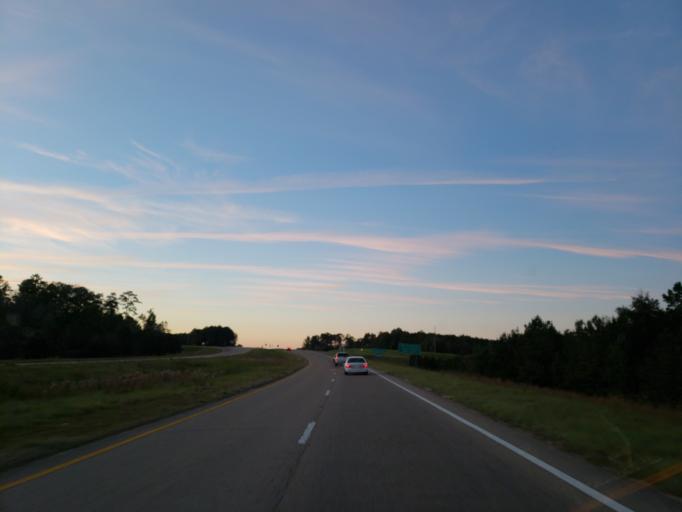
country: US
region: Mississippi
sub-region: Wayne County
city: Waynesboro
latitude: 31.6981
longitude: -88.6186
